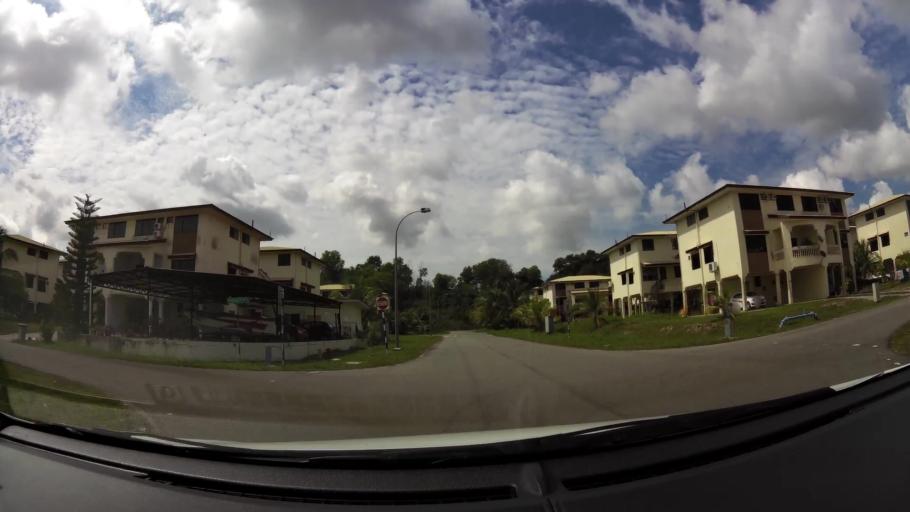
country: BN
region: Brunei and Muara
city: Bandar Seri Begawan
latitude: 4.9308
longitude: 114.8955
